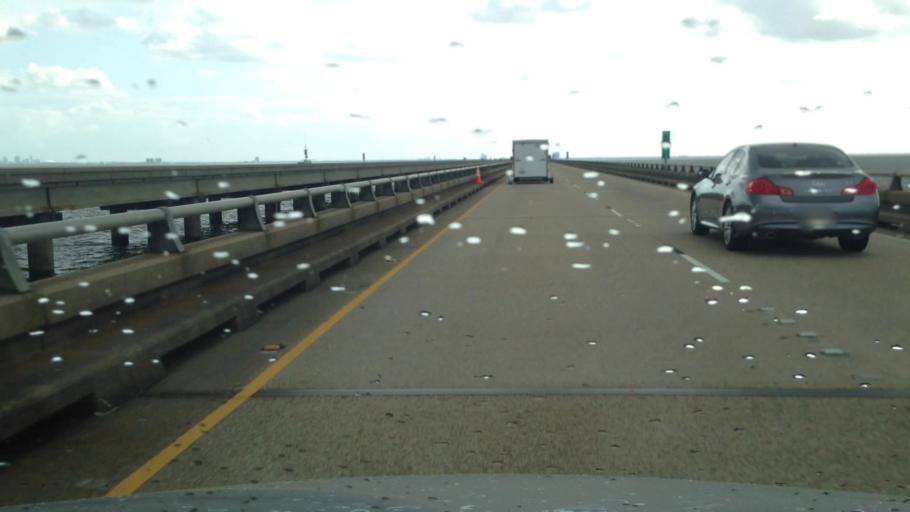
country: US
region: Louisiana
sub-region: Jefferson Parish
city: Metairie
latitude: 30.1069
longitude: -90.1392
